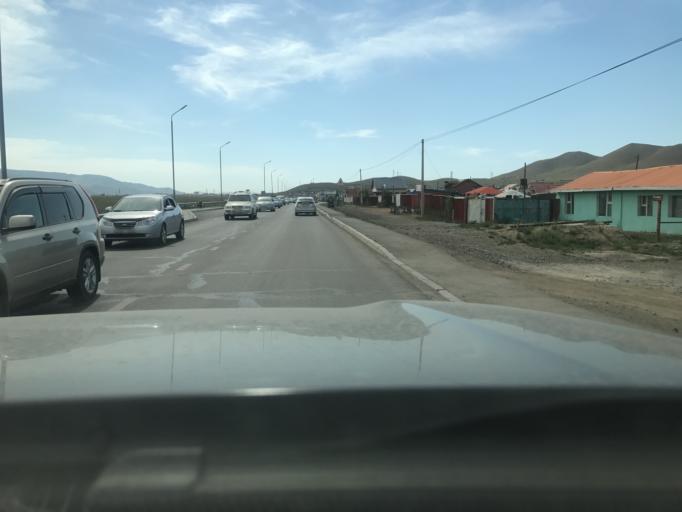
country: MN
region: Ulaanbaatar
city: Ulaanbaatar
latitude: 47.9158
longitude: 107.0780
